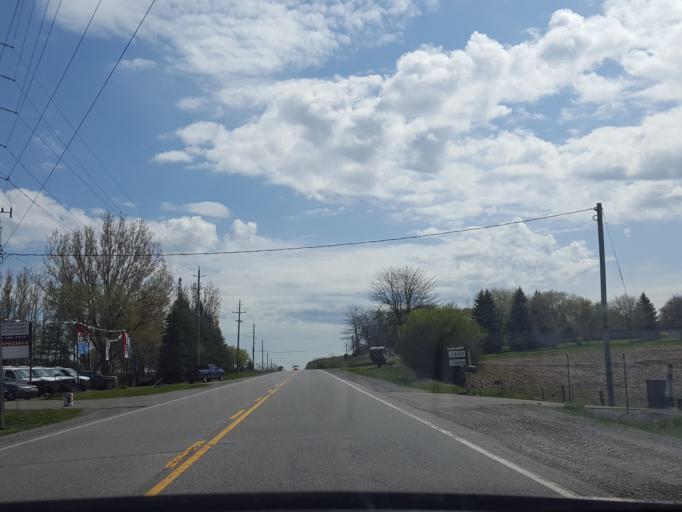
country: CA
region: Ontario
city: Oshawa
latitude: 44.1089
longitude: -78.8685
